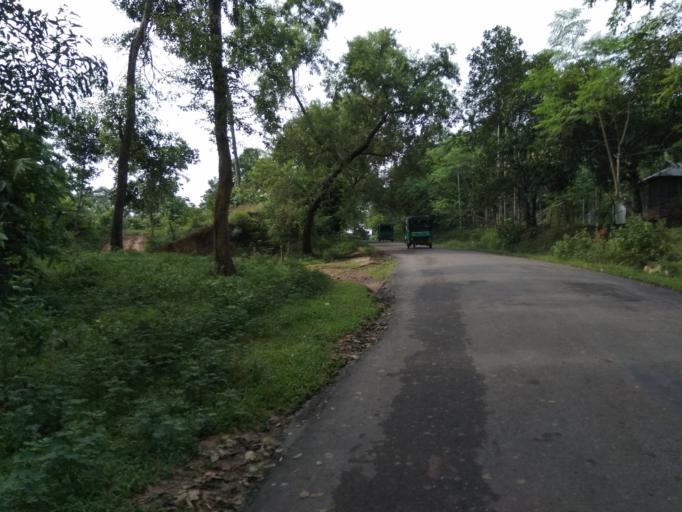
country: BD
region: Chittagong
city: Khagrachhari
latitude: 23.0039
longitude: 92.0113
